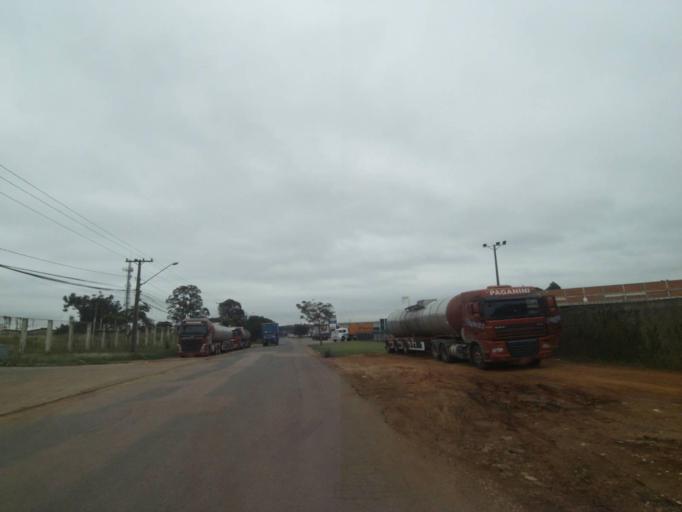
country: BR
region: Parana
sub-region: Araucaria
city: Araucaria
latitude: -25.5438
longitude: -49.3302
